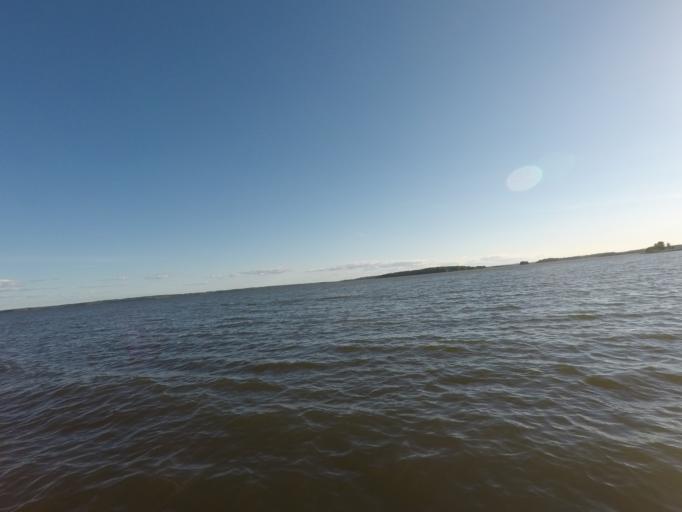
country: SE
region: Vaestmanland
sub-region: Vasteras
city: Vasteras
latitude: 59.5093
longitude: 16.5523
